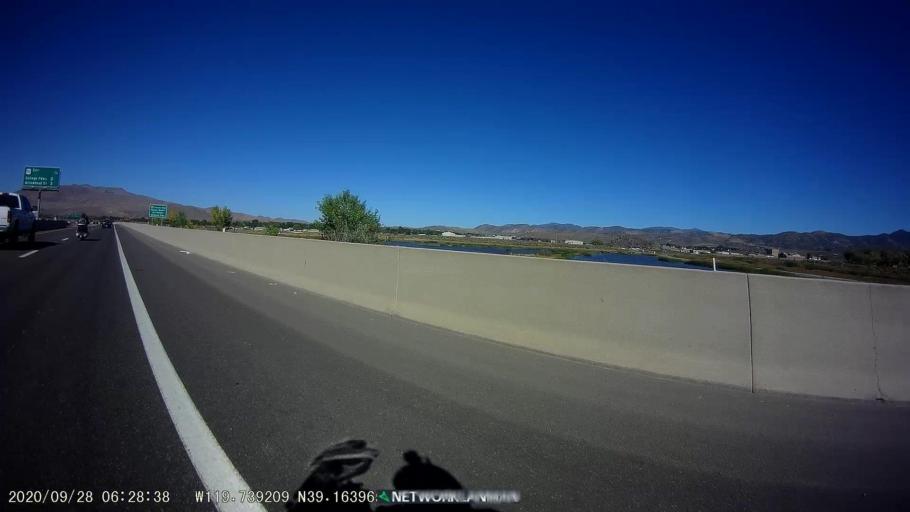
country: US
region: Nevada
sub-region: Carson City
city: Carson City
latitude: 39.1641
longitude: -119.7391
